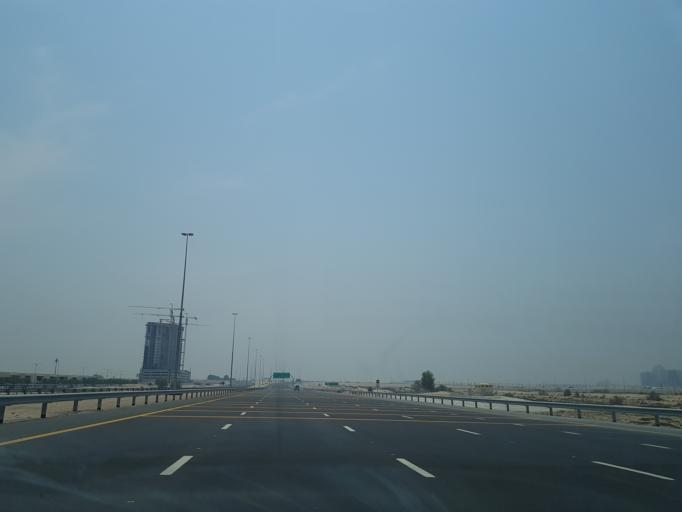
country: AE
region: Dubai
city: Dubai
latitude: 25.0298
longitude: 55.2494
